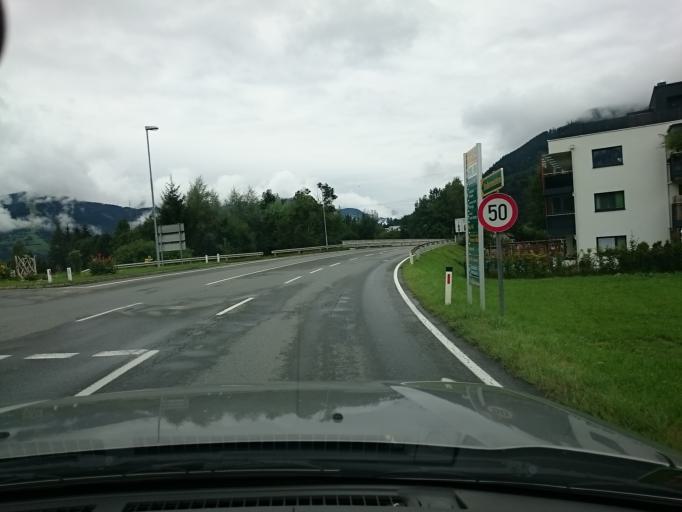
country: AT
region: Salzburg
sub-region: Politischer Bezirk Zell am See
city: Bruck an der Grossglocknerstrasse
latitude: 47.2791
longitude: 12.8253
